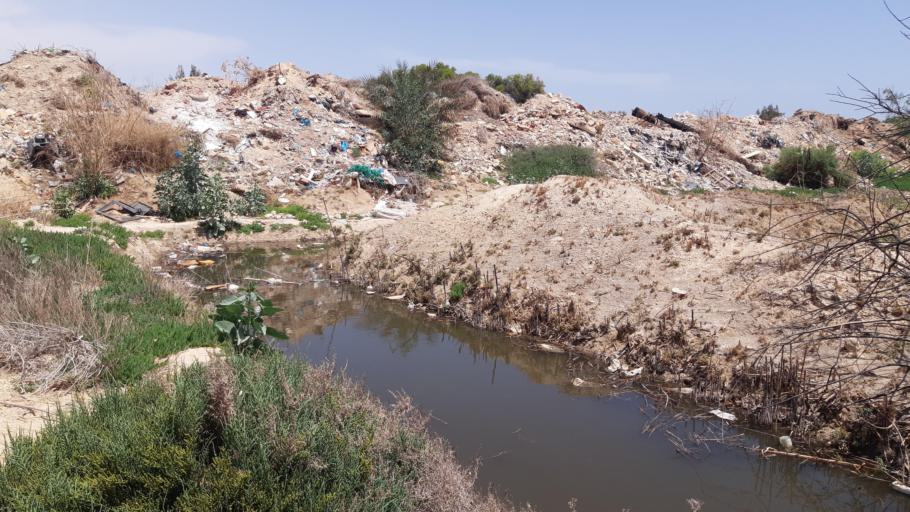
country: TN
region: Qabis
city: Gabes
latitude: 33.8755
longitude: 10.1074
